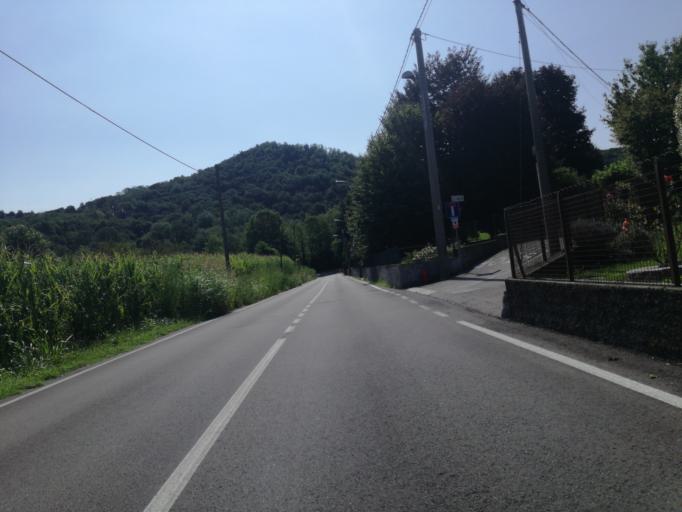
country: IT
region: Lombardy
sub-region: Provincia di Bergamo
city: Villa d'Adda
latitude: 45.7062
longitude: 9.4548
